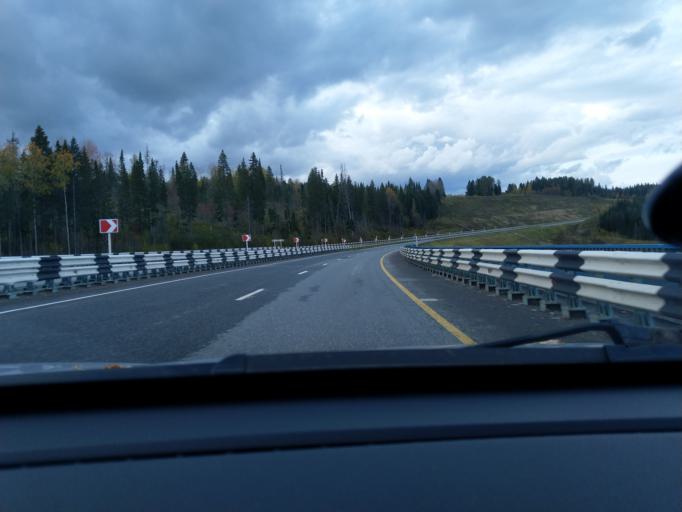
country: RU
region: Perm
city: Polazna
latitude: 58.3163
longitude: 56.4673
